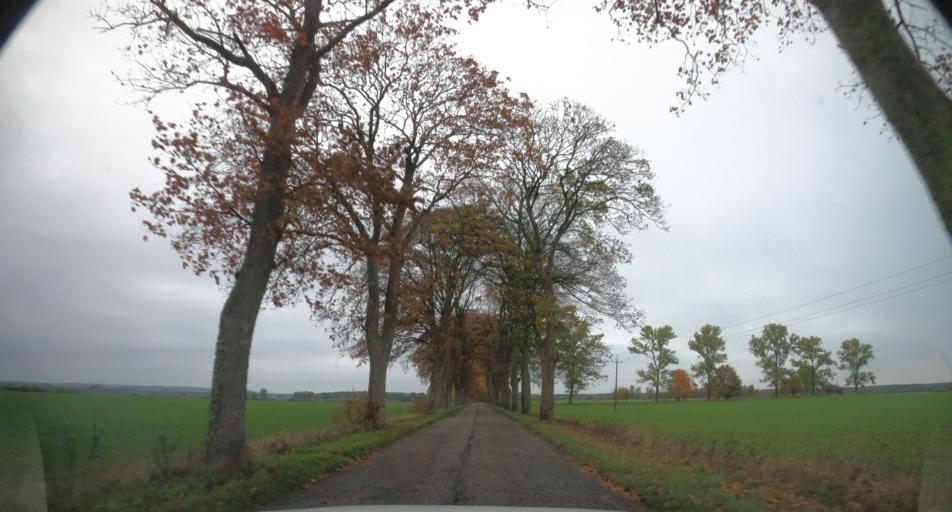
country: PL
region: West Pomeranian Voivodeship
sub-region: Powiat kamienski
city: Wolin
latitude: 53.9197
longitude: 14.6118
